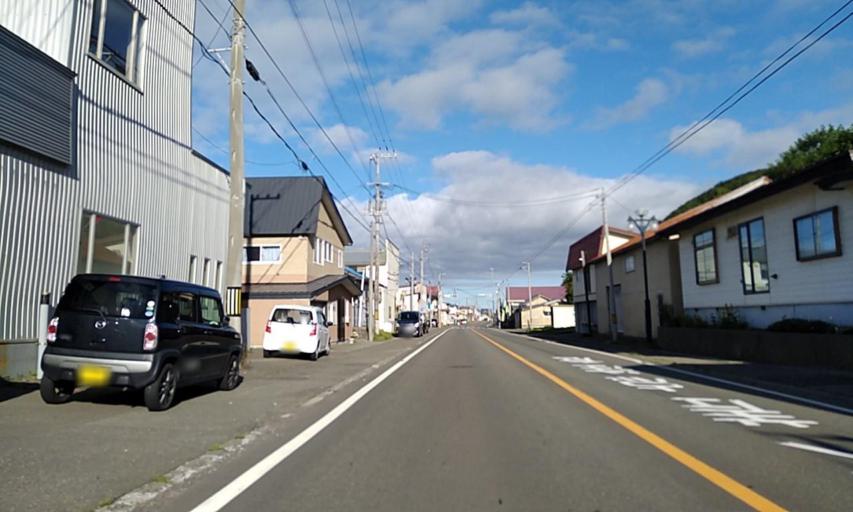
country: JP
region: Hokkaido
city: Shizunai-furukawacho
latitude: 42.1968
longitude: 142.6652
